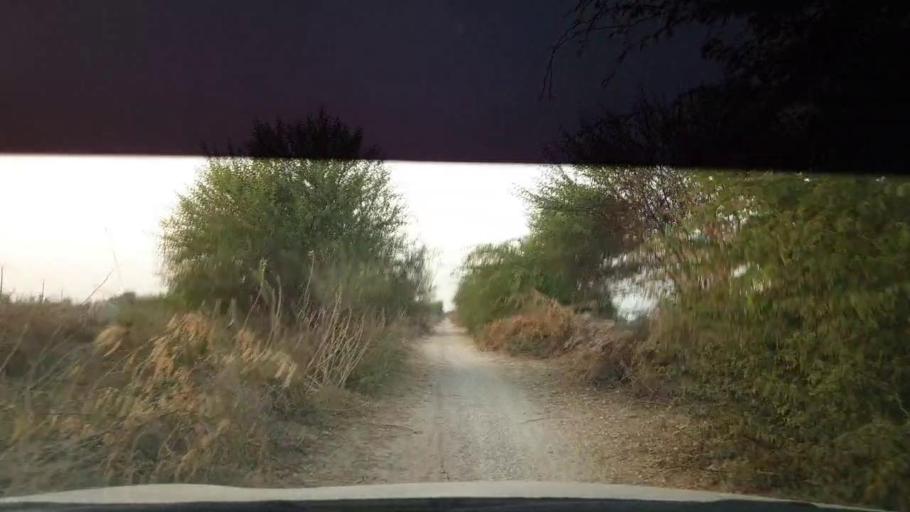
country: PK
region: Sindh
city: Berani
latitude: 25.7778
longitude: 68.9713
